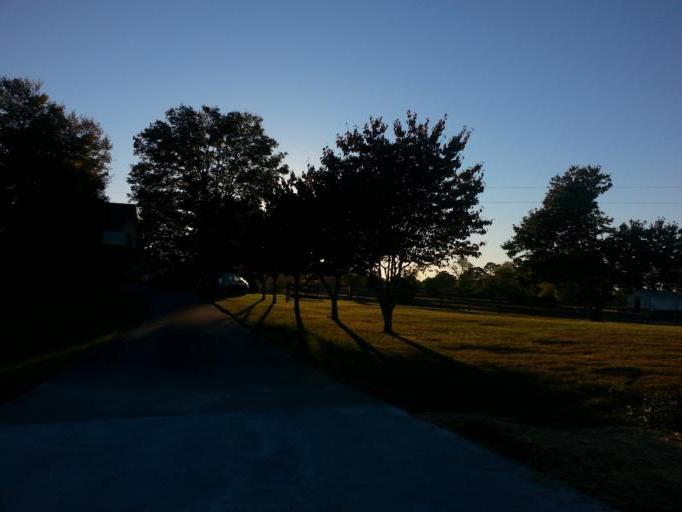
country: US
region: Tennessee
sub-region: Blount County
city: Wildwood
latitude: 35.8171
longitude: -83.7819
